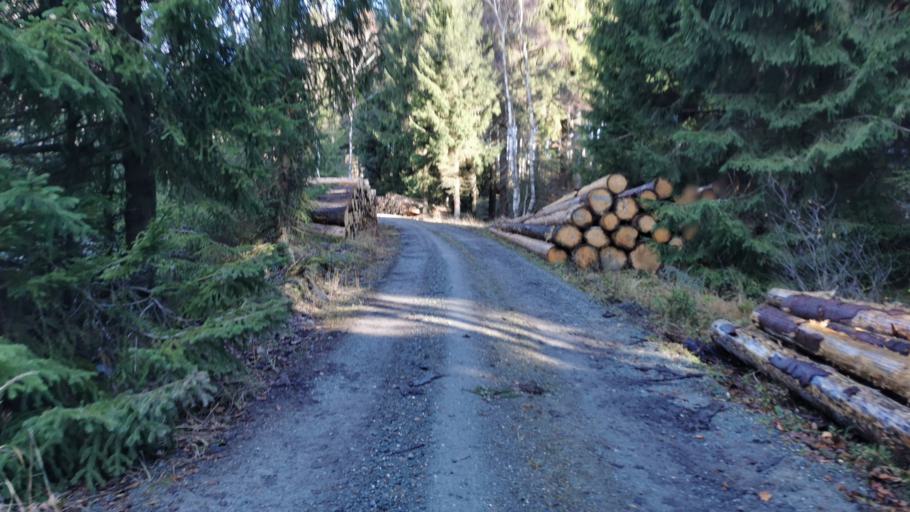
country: DE
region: Bavaria
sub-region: Upper Franconia
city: Reichenbach
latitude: 50.4580
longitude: 11.4392
